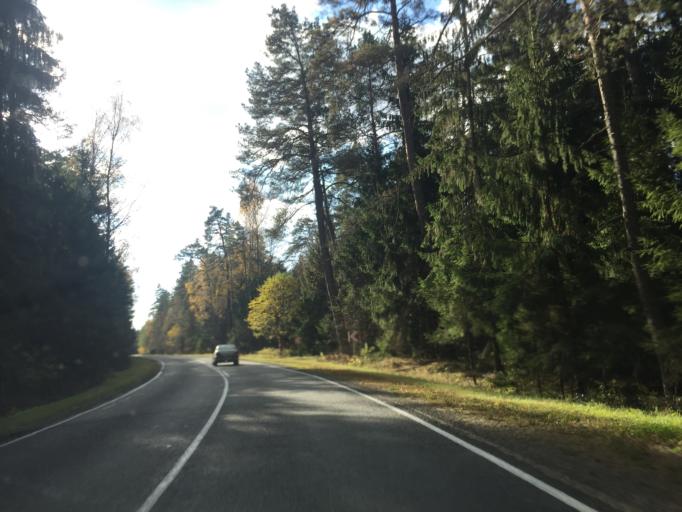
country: BY
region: Minsk
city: Narach
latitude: 54.9384
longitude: 26.5653
